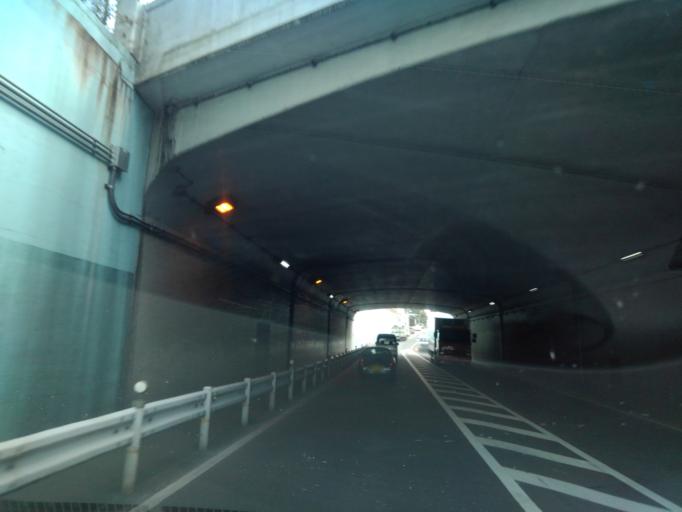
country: JP
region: Tokyo
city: Kokubunji
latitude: 35.7012
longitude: 139.4977
